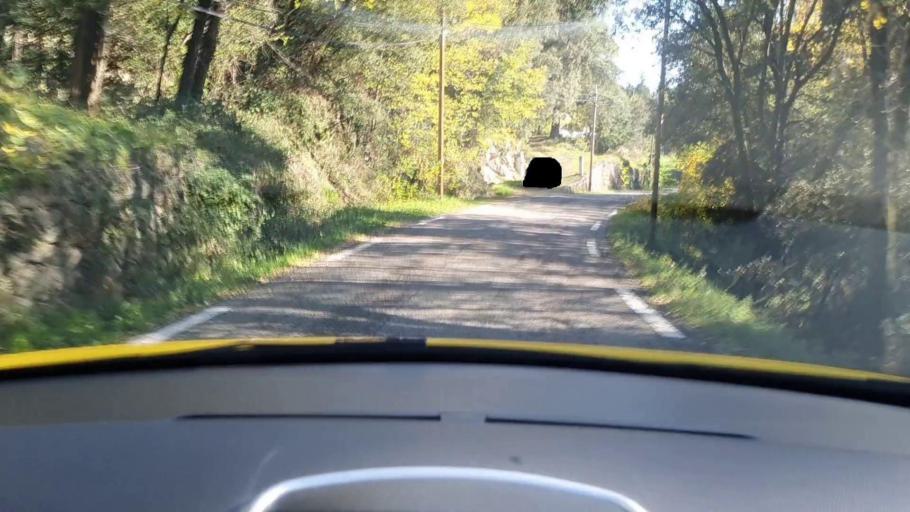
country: FR
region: Languedoc-Roussillon
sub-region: Departement du Gard
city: Lasalle
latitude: 44.0559
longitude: 3.8389
